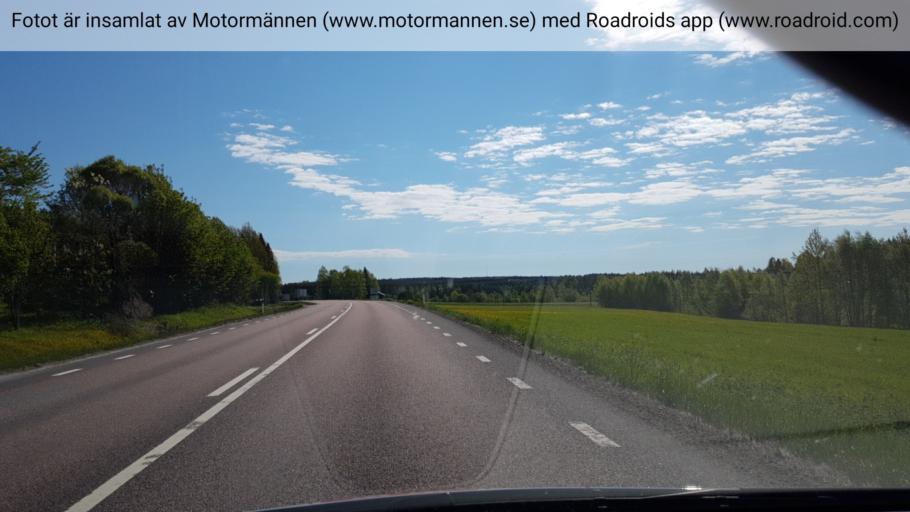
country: SE
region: Vaesterbotten
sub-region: Skelleftea Kommun
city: Burea
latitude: 64.3339
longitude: 21.2324
